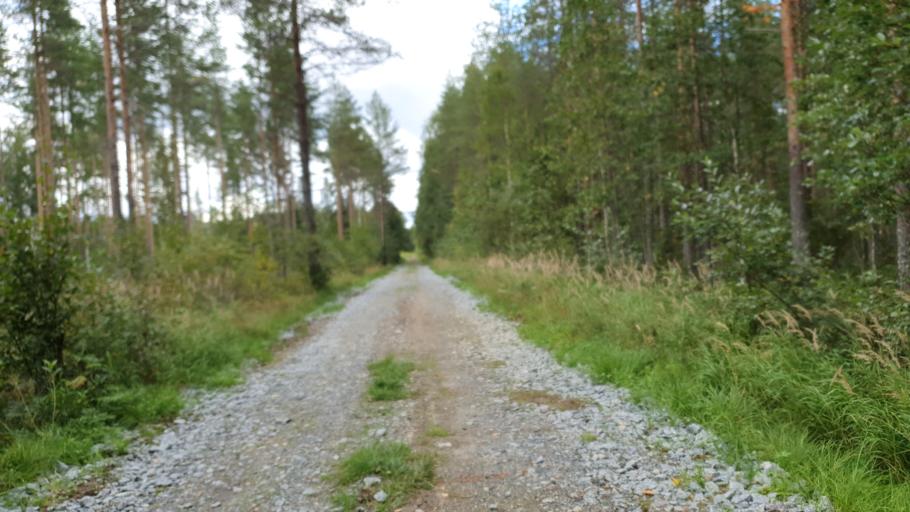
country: FI
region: Kainuu
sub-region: Kehys-Kainuu
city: Kuhmo
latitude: 64.1323
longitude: 29.4494
